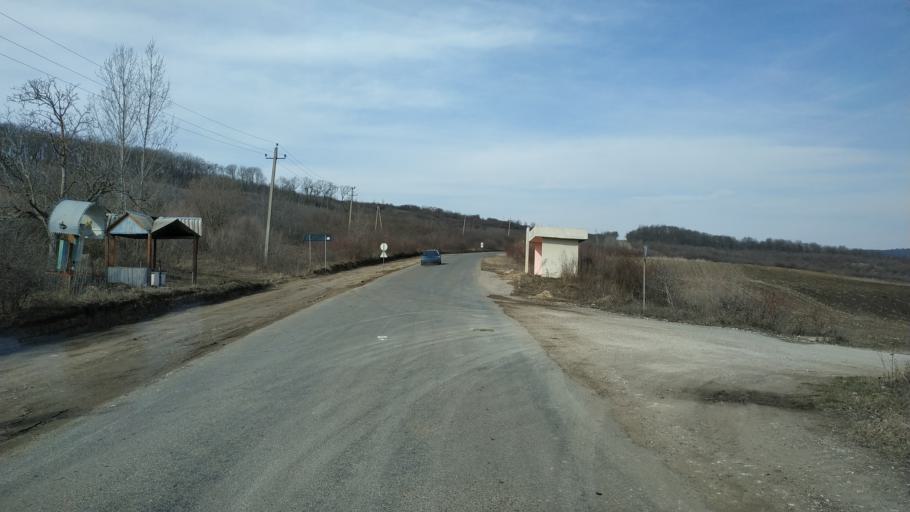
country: MD
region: Nisporeni
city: Nisporeni
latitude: 47.1848
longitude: 28.0737
